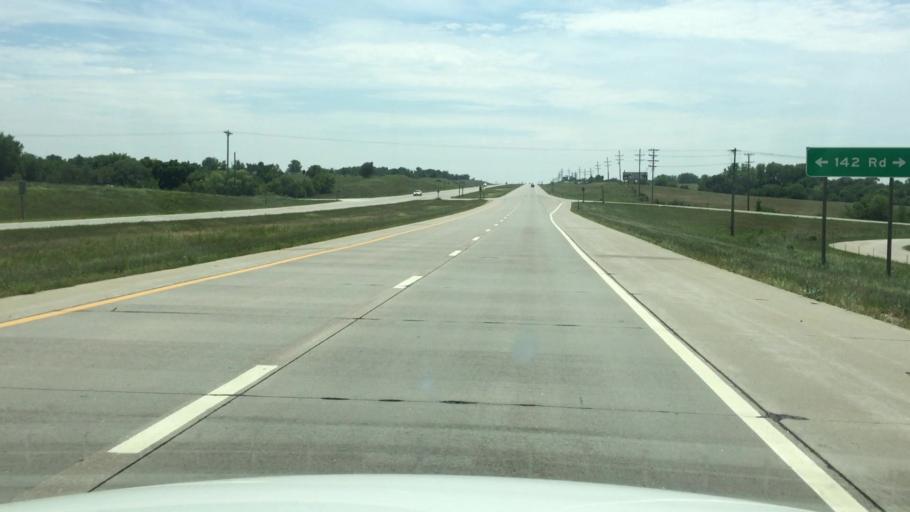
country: US
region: Kansas
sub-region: Jackson County
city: Holton
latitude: 39.3048
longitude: -95.7195
